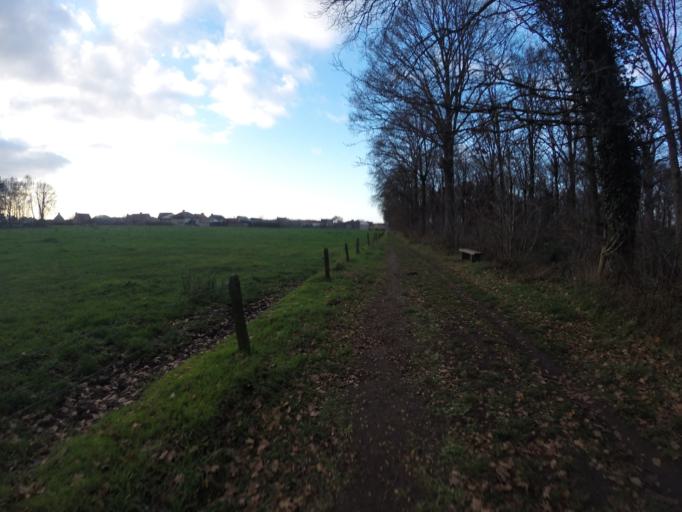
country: BE
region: Flanders
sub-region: Provincie West-Vlaanderen
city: Wingene
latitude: 51.0825
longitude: 3.3093
